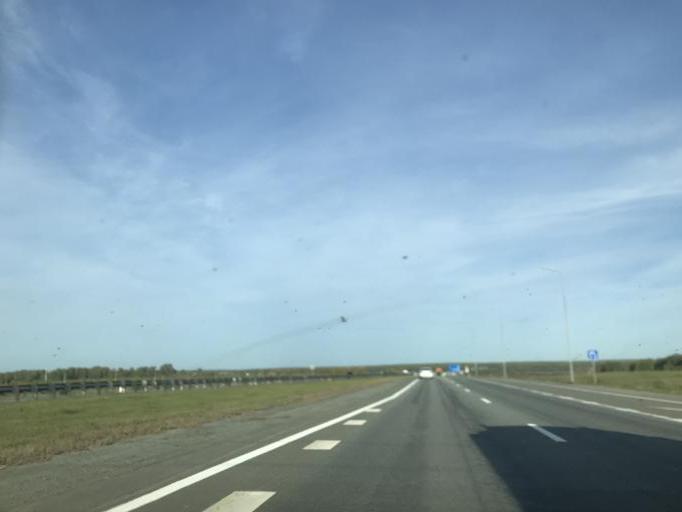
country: RU
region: Chelyabinsk
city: Poletayevo
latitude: 54.9822
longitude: 61.0157
